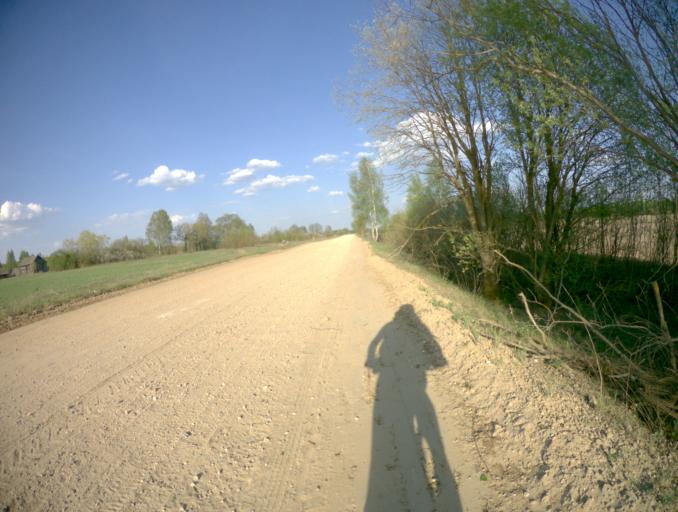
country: RU
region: Vladimir
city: Mstera
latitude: 56.5524
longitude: 41.7165
